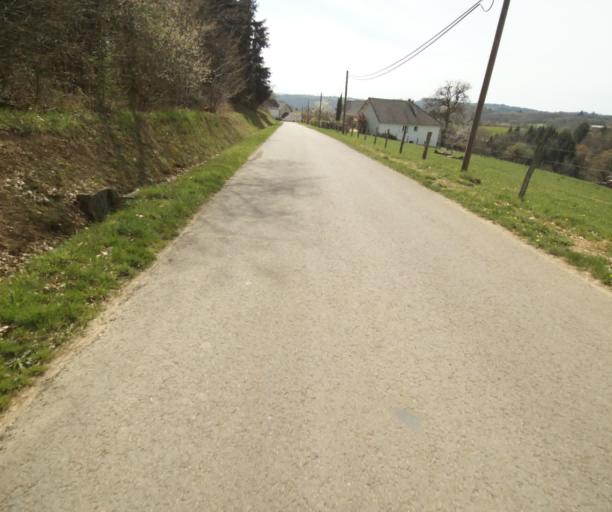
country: FR
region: Limousin
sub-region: Departement de la Correze
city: Naves
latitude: 45.3636
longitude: 1.8013
